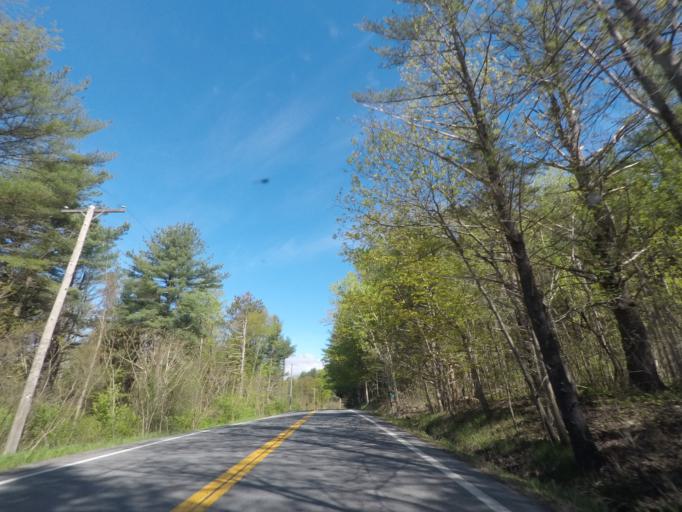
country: US
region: New York
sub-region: Albany County
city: Ravena
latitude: 42.4996
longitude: -73.9448
